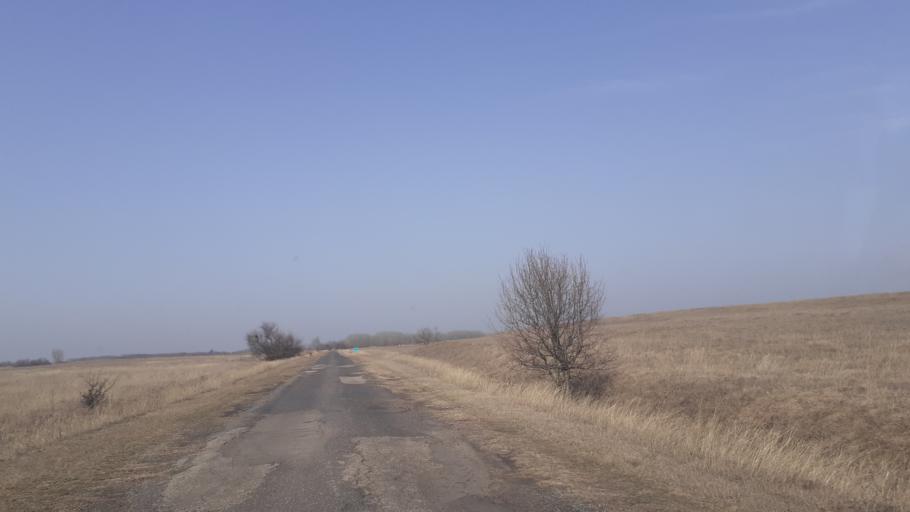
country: HU
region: Pest
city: Dabas
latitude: 47.1015
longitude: 19.2279
